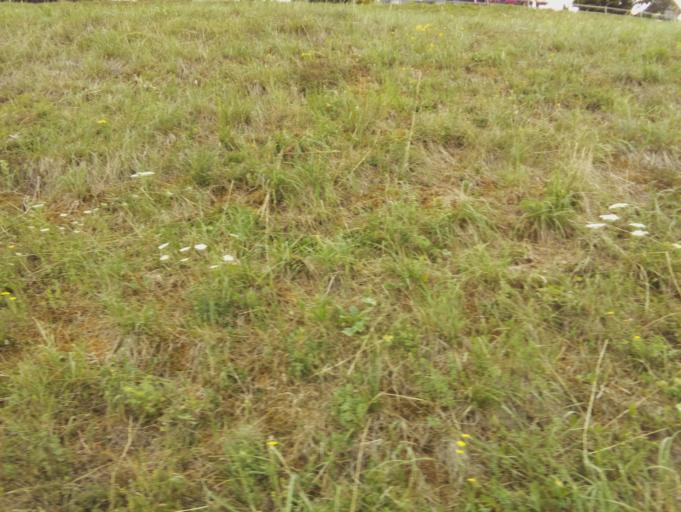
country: CH
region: Saint Gallen
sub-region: Wahlkreis Toggenburg
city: Lutisburg
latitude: 47.4004
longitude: 9.0815
